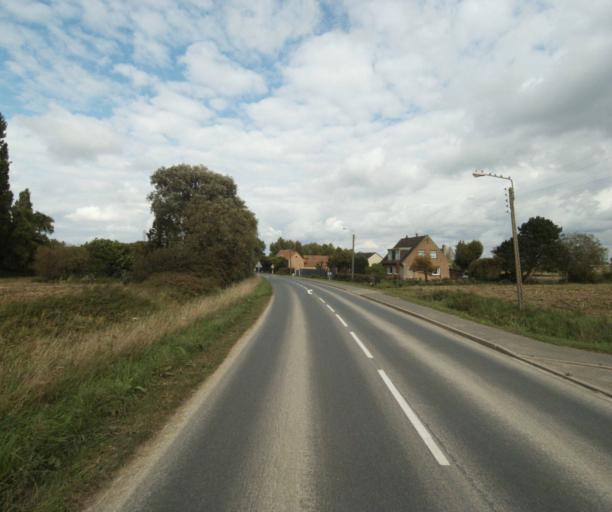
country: FR
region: Nord-Pas-de-Calais
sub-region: Departement du Nord
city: Premesques
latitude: 50.6691
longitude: 2.9468
